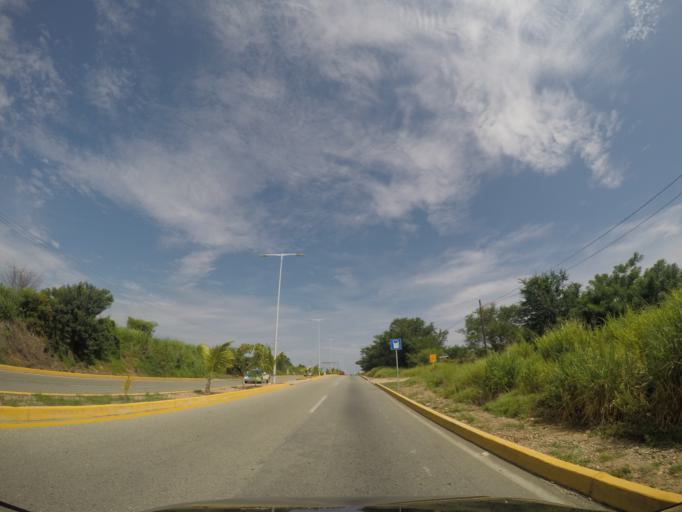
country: MX
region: Oaxaca
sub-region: Santa Maria Colotepec
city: Brisas de Zicatela
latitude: 15.8348
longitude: -97.0369
